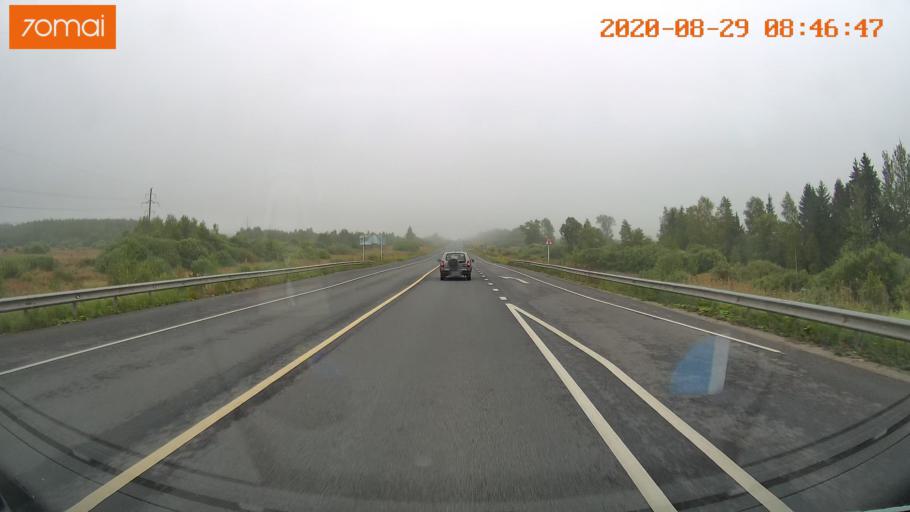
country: RU
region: Ivanovo
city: Rodniki
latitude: 57.1436
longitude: 41.8219
